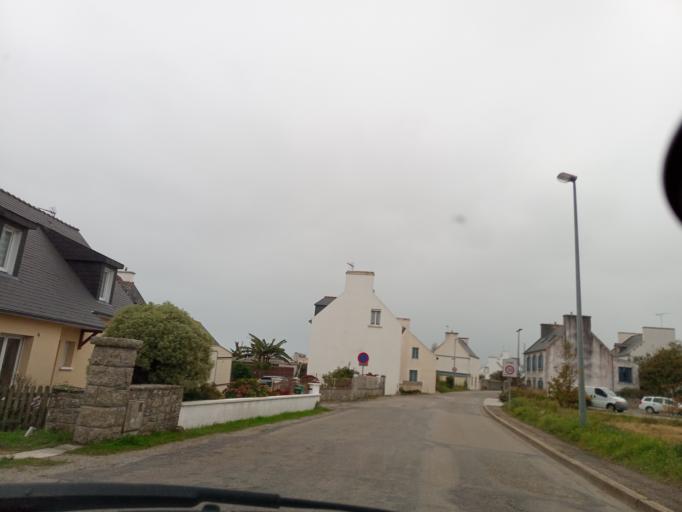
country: FR
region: Brittany
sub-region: Departement du Finistere
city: Esquibien
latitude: 48.0239
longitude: -4.5592
